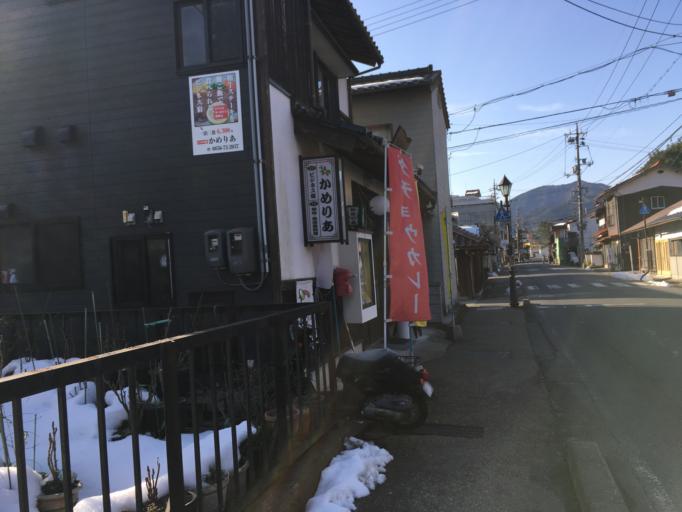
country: JP
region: Shimane
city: Masuda
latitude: 34.4704
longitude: 131.7734
